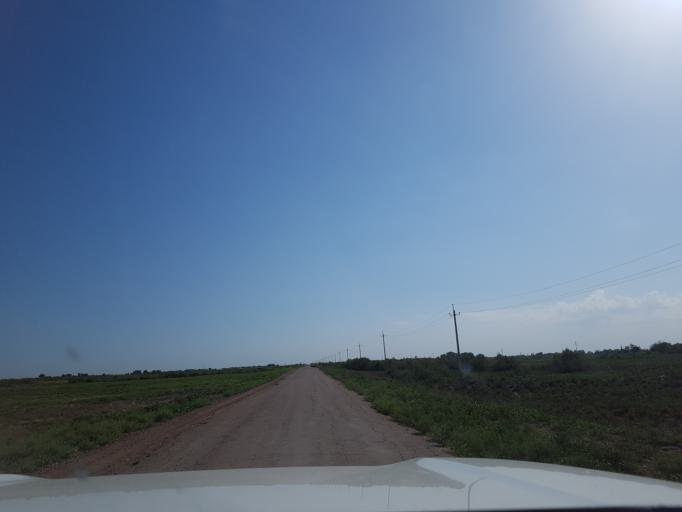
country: TM
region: Dasoguz
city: Koeneuergench
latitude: 42.0555
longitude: 58.8377
